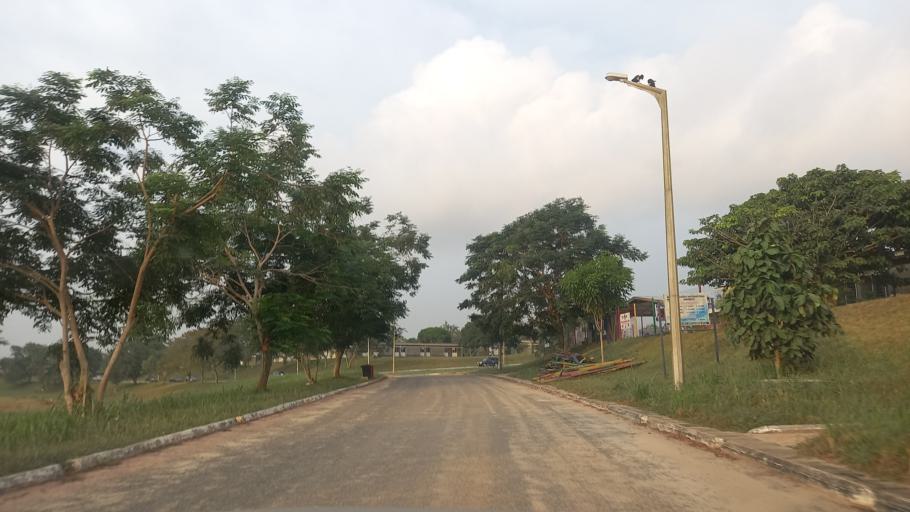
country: GH
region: Western
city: Shama Junction
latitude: 4.9843
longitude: -1.6585
